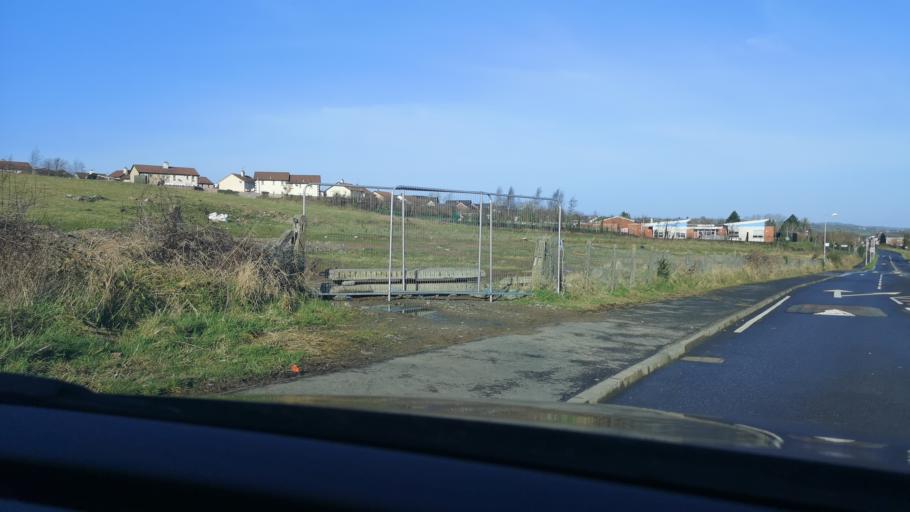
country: GB
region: Northern Ireland
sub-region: Newry and Mourne District
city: Newry
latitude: 54.1755
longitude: -6.3530
